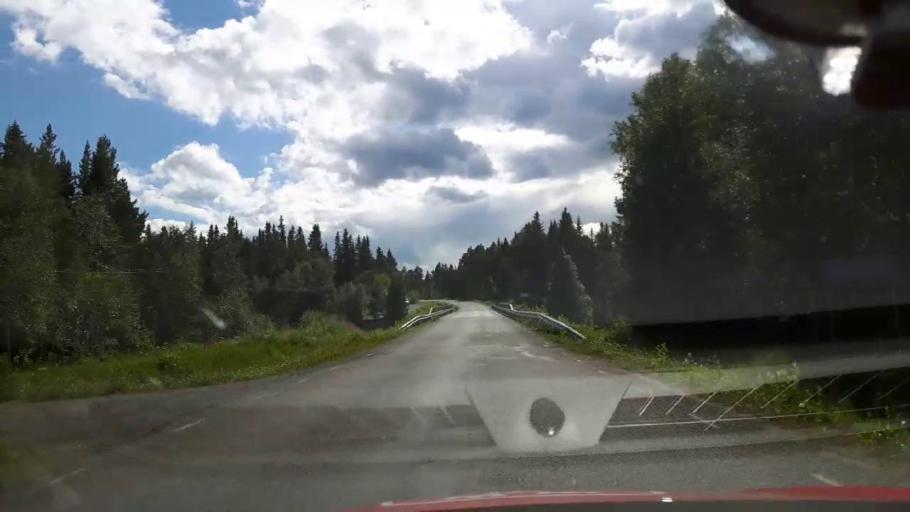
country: SE
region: Jaemtland
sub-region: Are Kommun
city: Are
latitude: 63.1934
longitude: 13.1349
